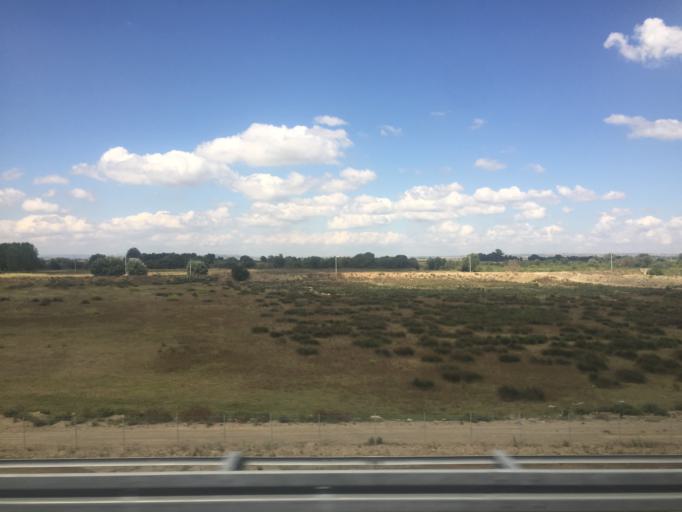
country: TR
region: Bursa
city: Tatkavakli
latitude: 40.1126
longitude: 28.2771
